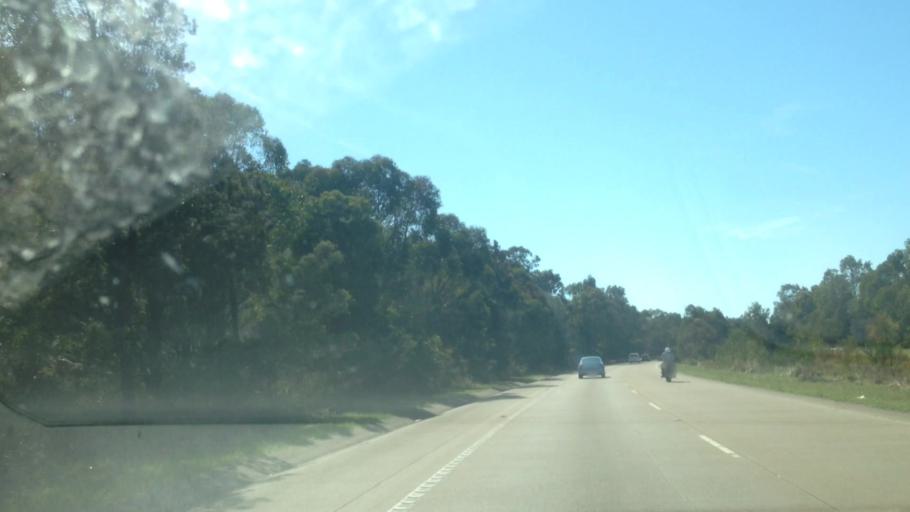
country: AU
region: New South Wales
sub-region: Lake Macquarie Shire
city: Holmesville
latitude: -32.8959
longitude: 151.5745
